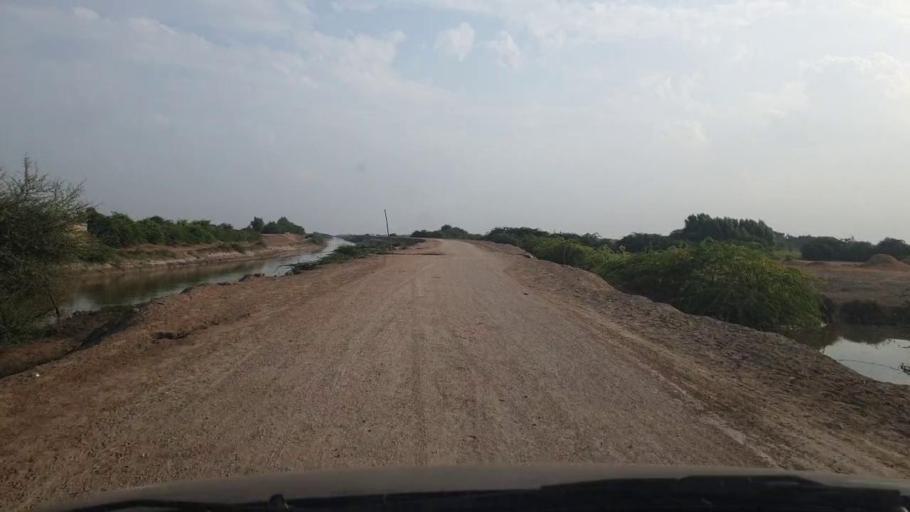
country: PK
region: Sindh
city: Badin
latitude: 24.5492
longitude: 68.6711
